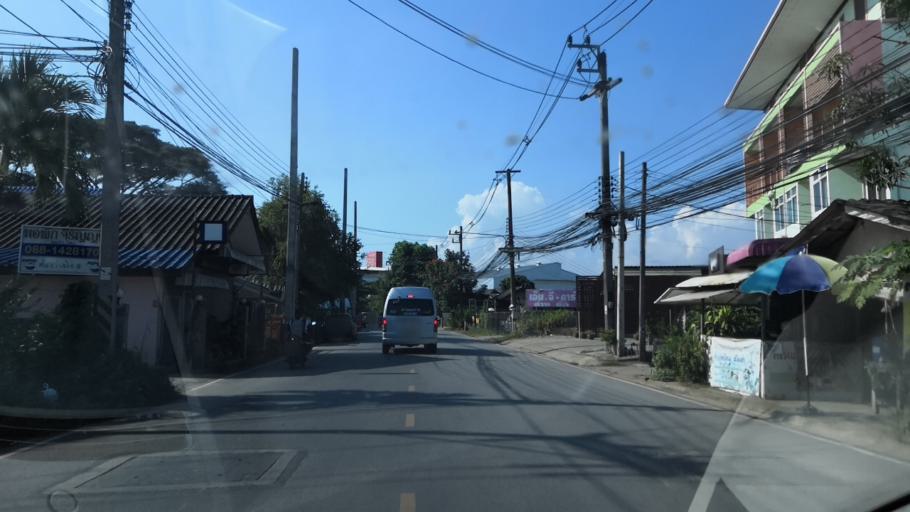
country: TH
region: Chiang Rai
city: Chiang Rai
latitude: 19.9286
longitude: 99.8467
